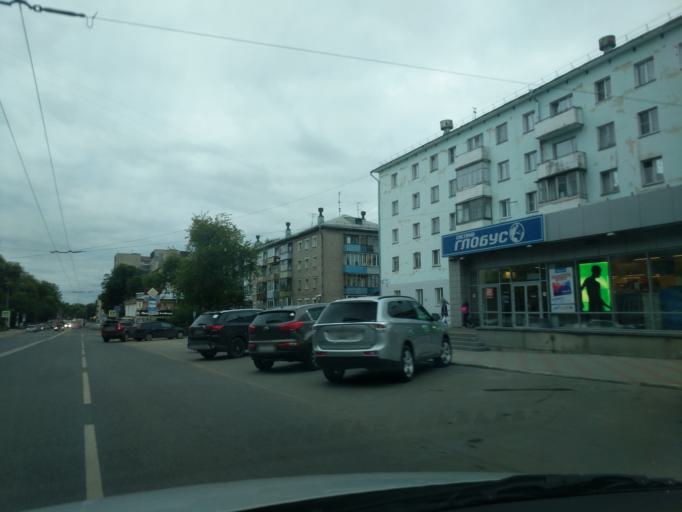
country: RU
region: Kirov
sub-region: Kirovo-Chepetskiy Rayon
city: Kirov
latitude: 58.6094
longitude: 49.6678
